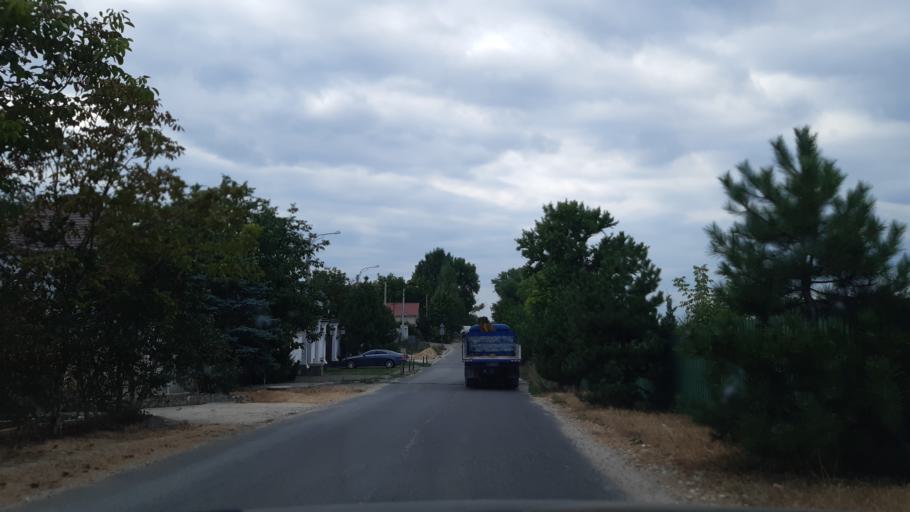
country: MD
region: Chisinau
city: Vatra
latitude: 47.0521
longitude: 28.7339
